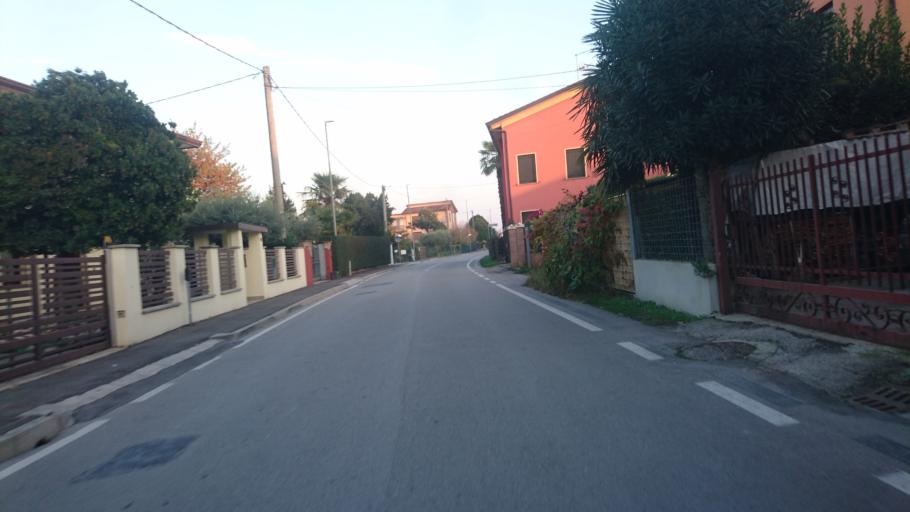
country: IT
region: Veneto
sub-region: Provincia di Padova
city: Abano Terme
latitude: 45.3513
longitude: 11.8125
